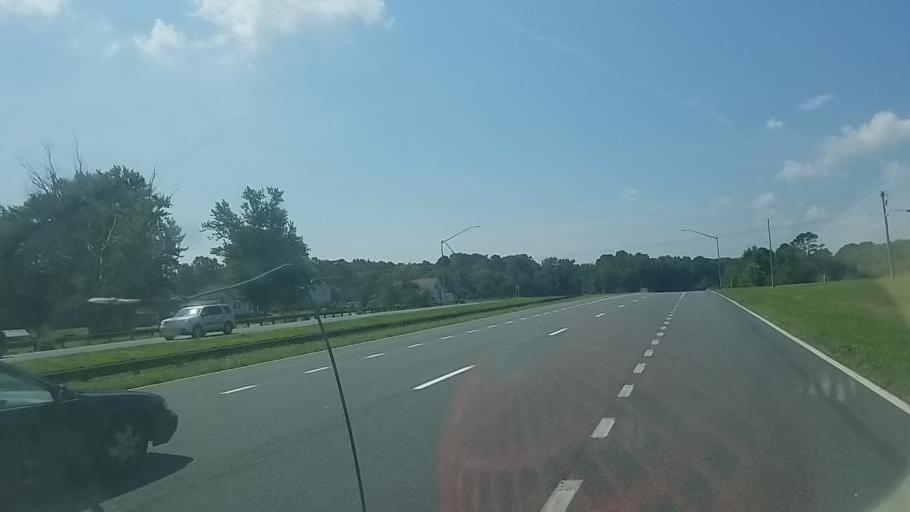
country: US
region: Maryland
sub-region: Worcester County
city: Berlin
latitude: 38.2853
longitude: -75.2312
